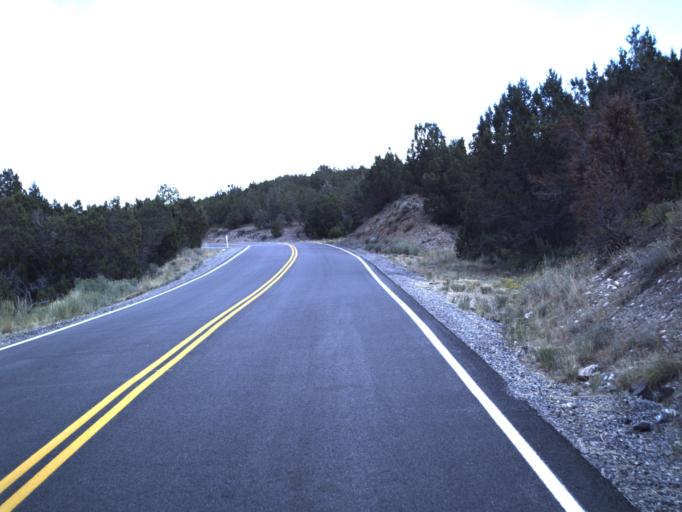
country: US
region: Utah
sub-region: Tooele County
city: Grantsville
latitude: 40.3406
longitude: -112.5779
